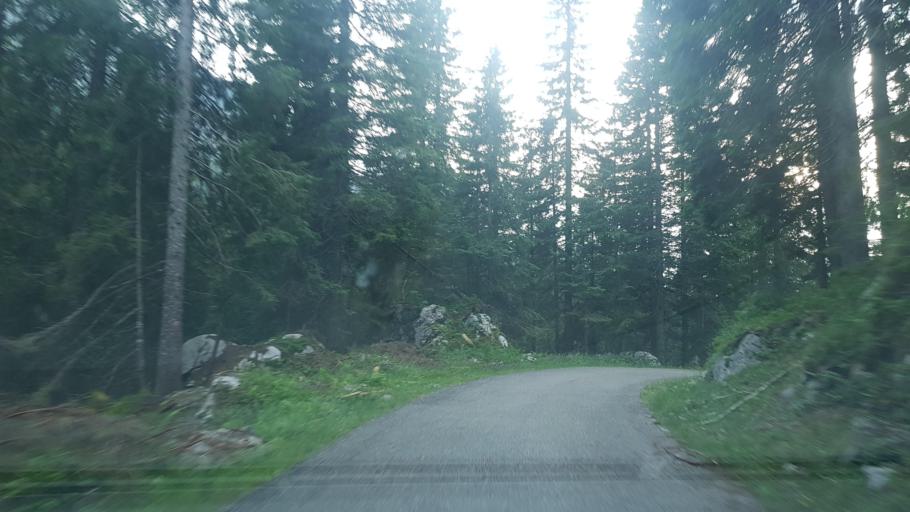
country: IT
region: Friuli Venezia Giulia
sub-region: Provincia di Udine
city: Paularo
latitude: 46.5728
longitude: 13.1598
